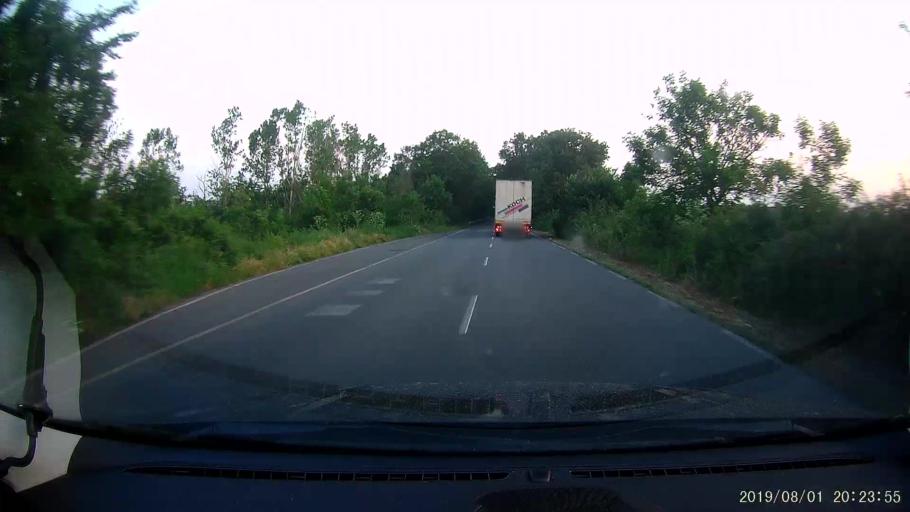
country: BG
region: Yambol
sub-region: Obshtina Elkhovo
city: Elkhovo
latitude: 42.2399
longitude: 26.5969
